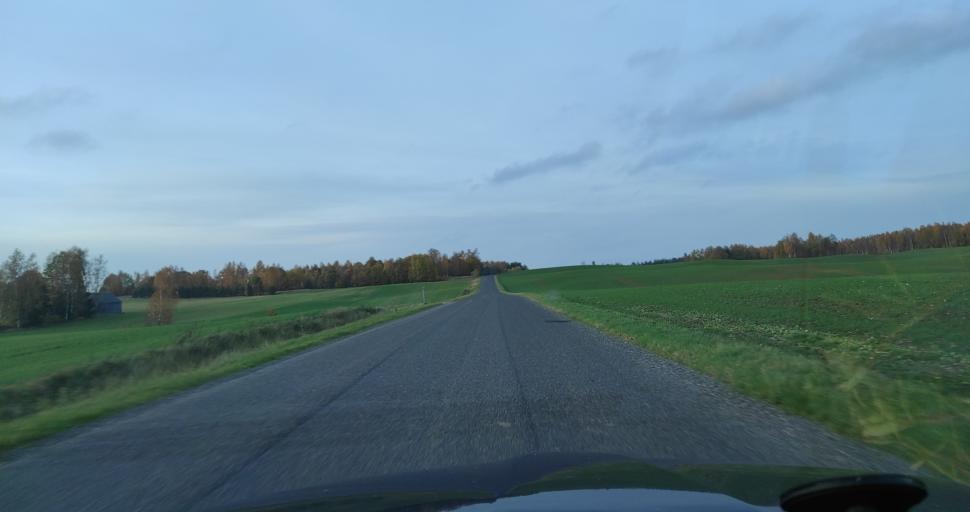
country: LV
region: Aizpute
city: Aizpute
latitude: 56.7028
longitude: 21.7946
